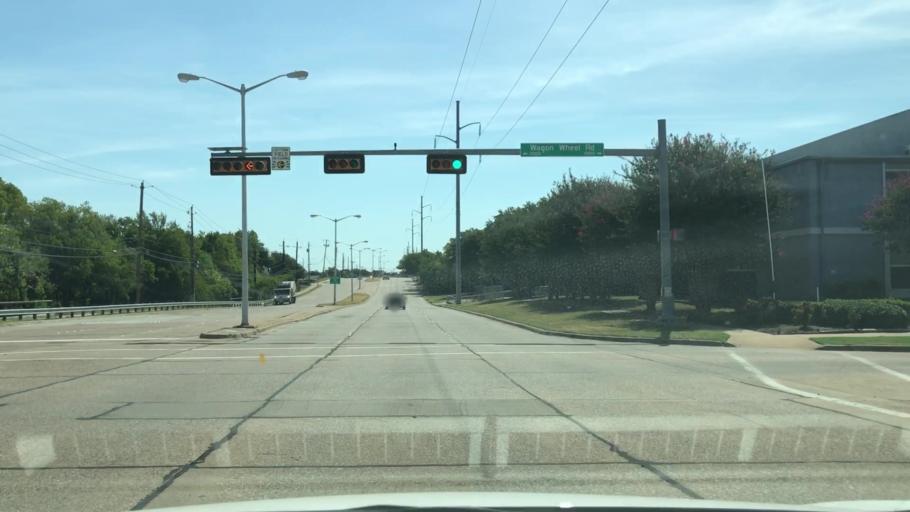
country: US
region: Texas
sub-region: Dallas County
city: Garland
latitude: 32.9451
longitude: -96.6536
